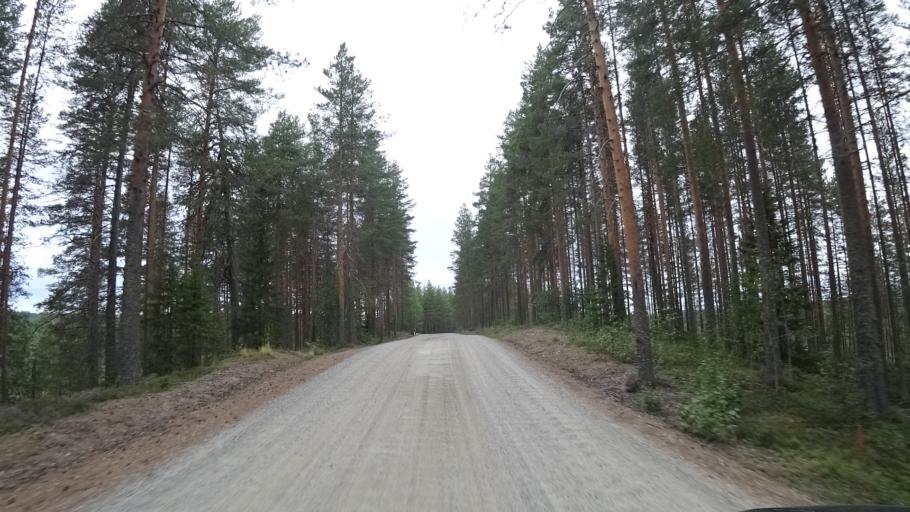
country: FI
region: North Karelia
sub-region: Pielisen Karjala
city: Lieksa
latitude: 63.2338
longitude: 30.3663
